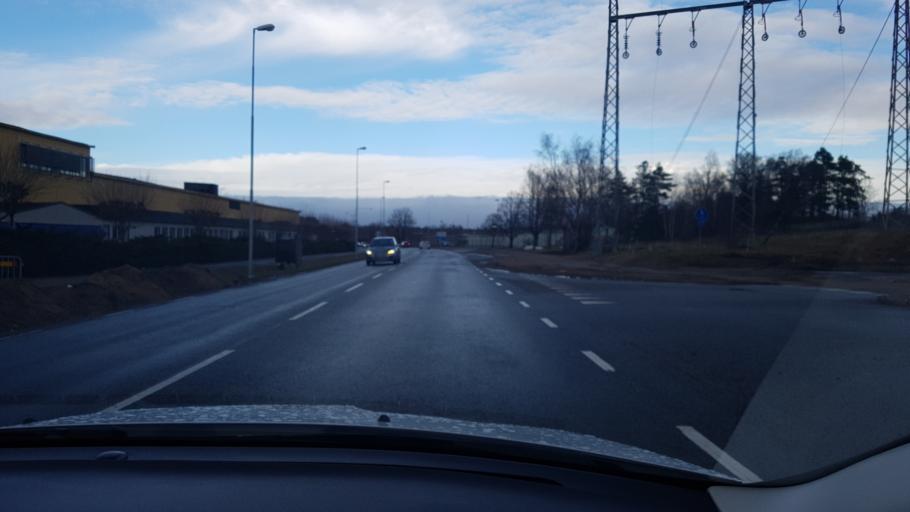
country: SE
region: Skane
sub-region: Hassleholms Kommun
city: Hassleholm
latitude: 56.1636
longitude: 13.7863
